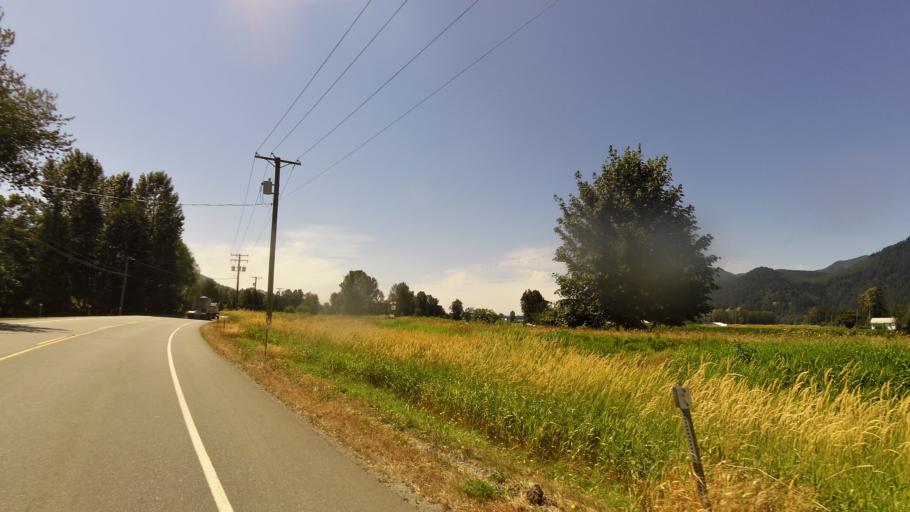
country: CA
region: British Columbia
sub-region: Fraser Valley Regional District
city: Chilliwack
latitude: 49.1740
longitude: -122.0821
